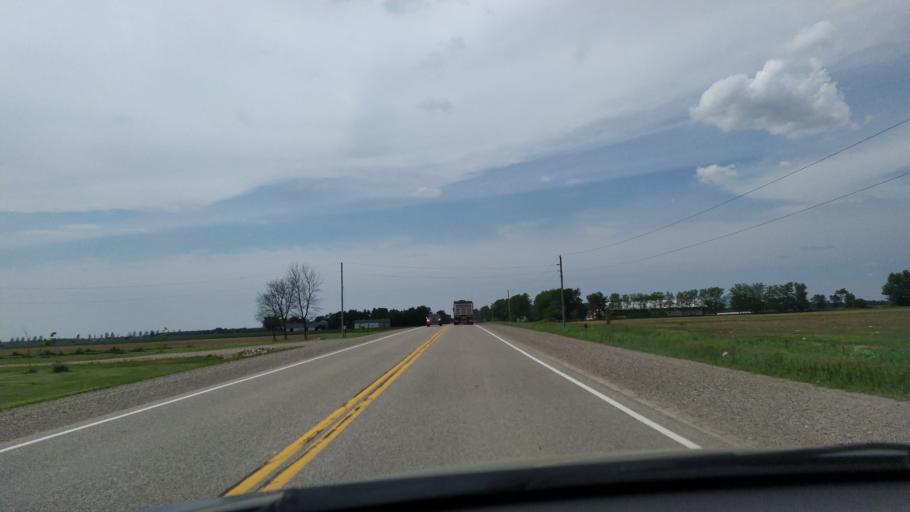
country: CA
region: Ontario
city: Stratford
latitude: 43.2305
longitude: -81.0762
